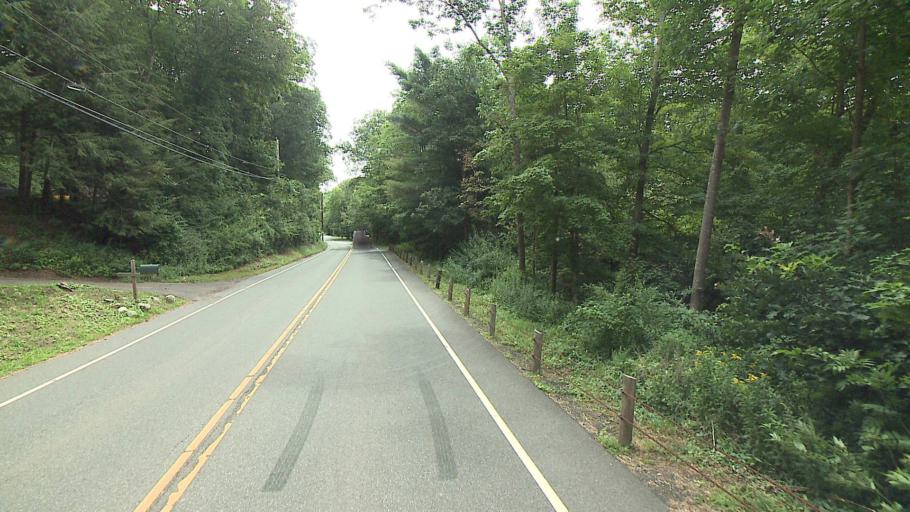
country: US
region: Connecticut
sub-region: Litchfield County
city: Woodbury
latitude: 41.5711
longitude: -73.2307
